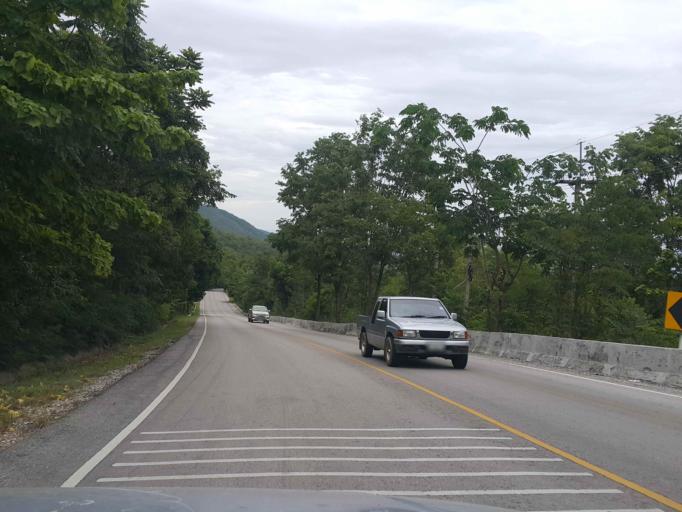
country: TH
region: Lampang
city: Thoen
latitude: 17.6457
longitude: 99.2954
